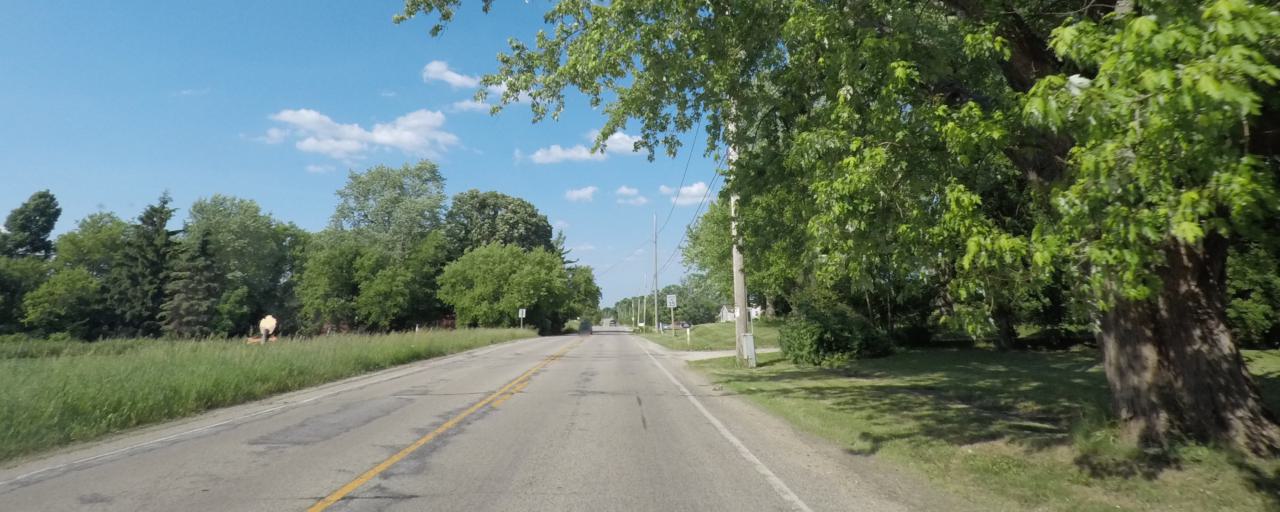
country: US
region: Wisconsin
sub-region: Waukesha County
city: Mukwonago
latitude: 42.8368
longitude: -88.2751
